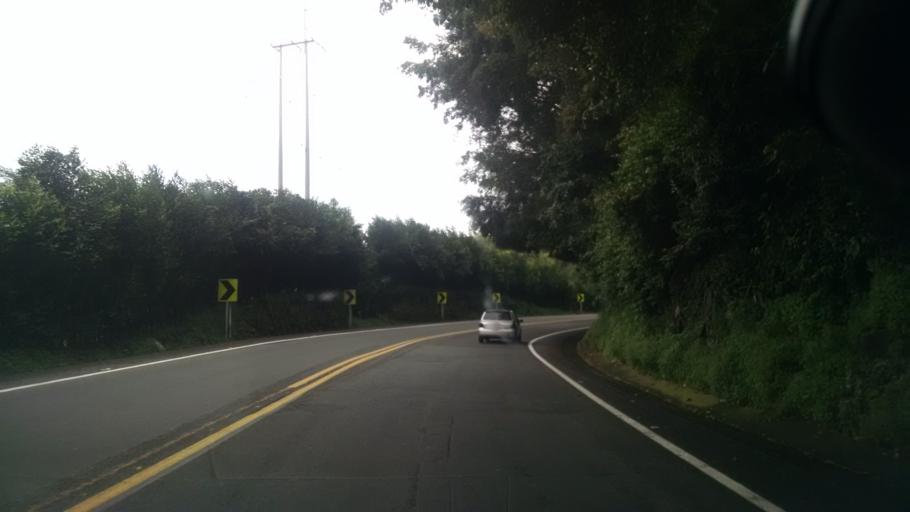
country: CO
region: Caldas
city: Palestina
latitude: 5.0244
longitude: -75.5975
